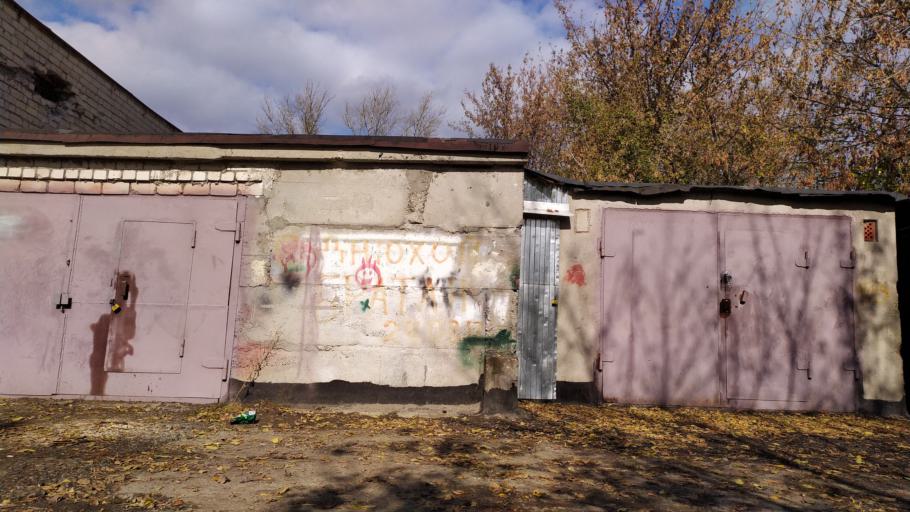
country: RU
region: Kursk
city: Kursk
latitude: 51.6513
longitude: 36.1439
